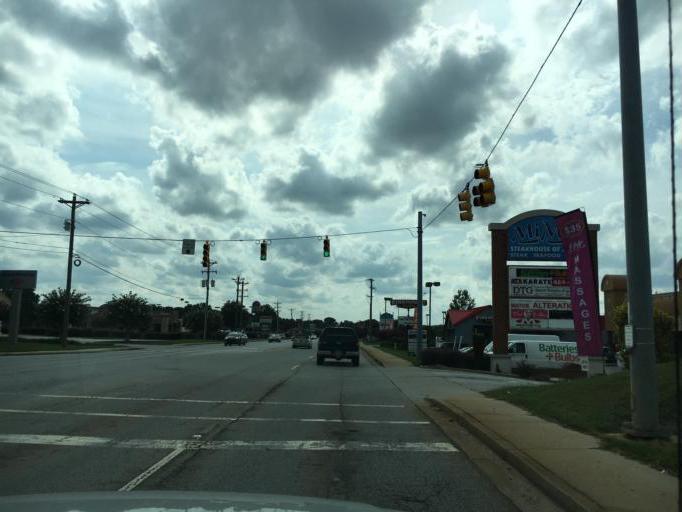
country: US
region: South Carolina
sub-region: Greenville County
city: Five Forks
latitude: 34.8198
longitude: -82.2691
